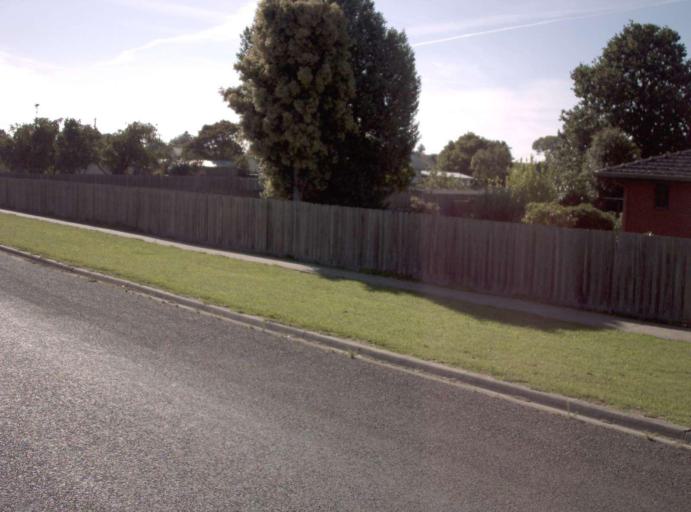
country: AU
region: Victoria
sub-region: East Gippsland
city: Lakes Entrance
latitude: -37.6978
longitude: 148.4608
